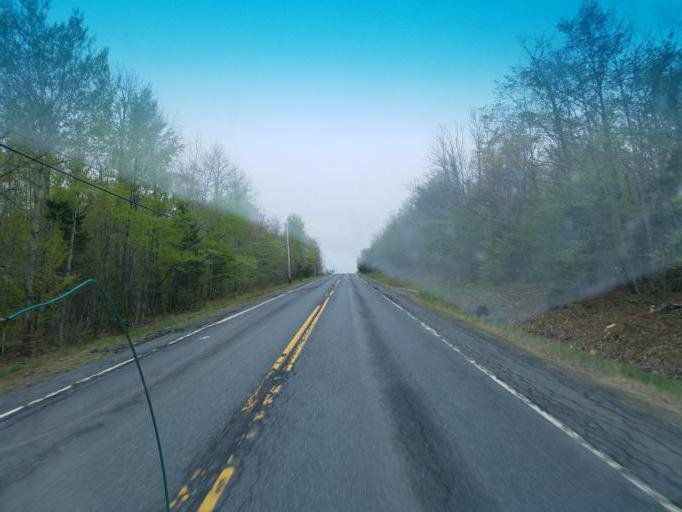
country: US
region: Maine
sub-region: Aroostook County
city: Hodgdon
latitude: 45.9119
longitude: -67.8347
